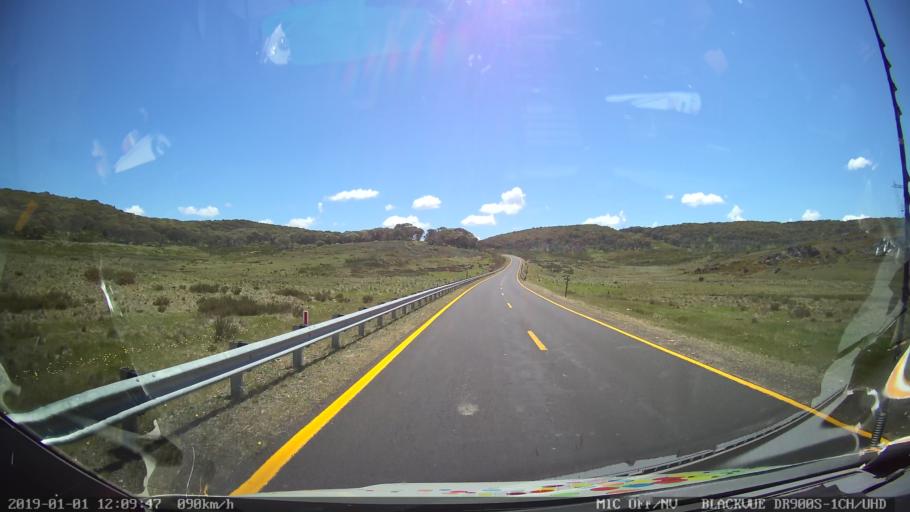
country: AU
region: New South Wales
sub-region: Tumut Shire
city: Tumut
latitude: -35.8037
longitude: 148.4970
